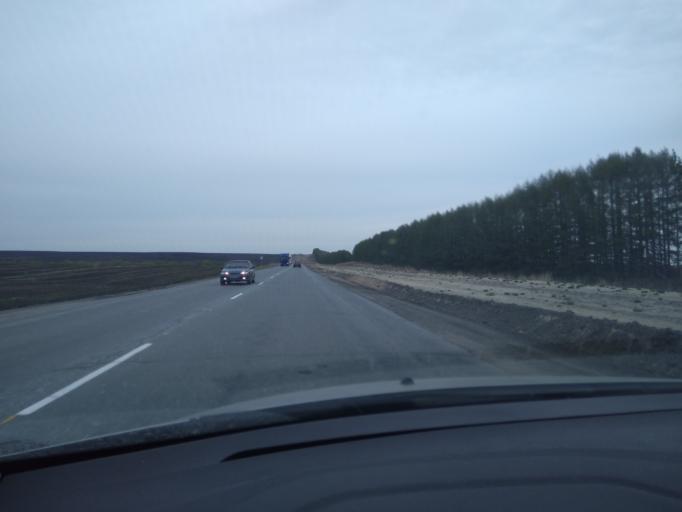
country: RU
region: Sverdlovsk
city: Kamyshlov
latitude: 56.8567
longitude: 62.8846
